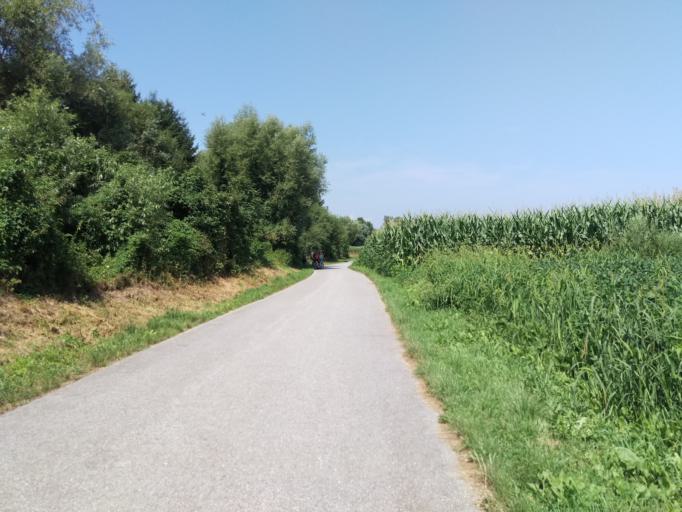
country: AT
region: Styria
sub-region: Politischer Bezirk Graz-Umgebung
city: Gossendorf
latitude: 46.9940
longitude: 15.4608
